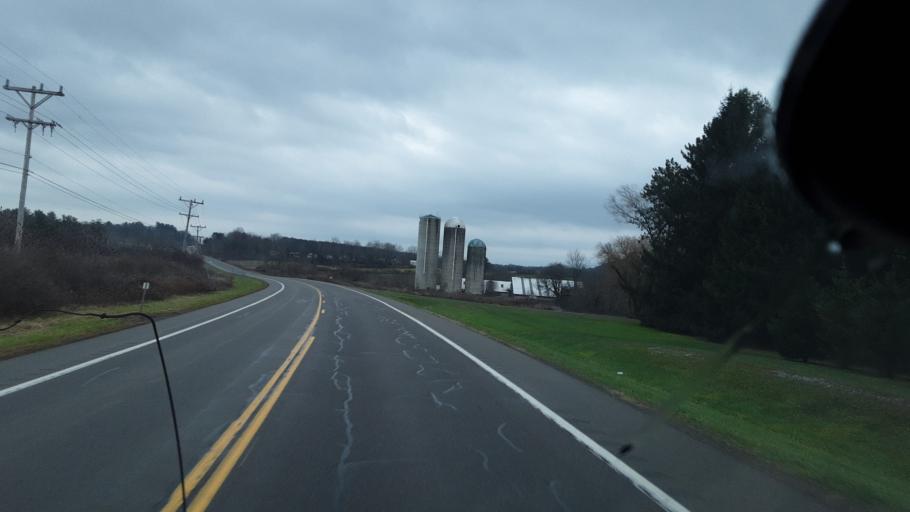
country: US
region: New York
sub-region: Allegany County
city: Houghton
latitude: 42.3890
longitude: -78.2084
